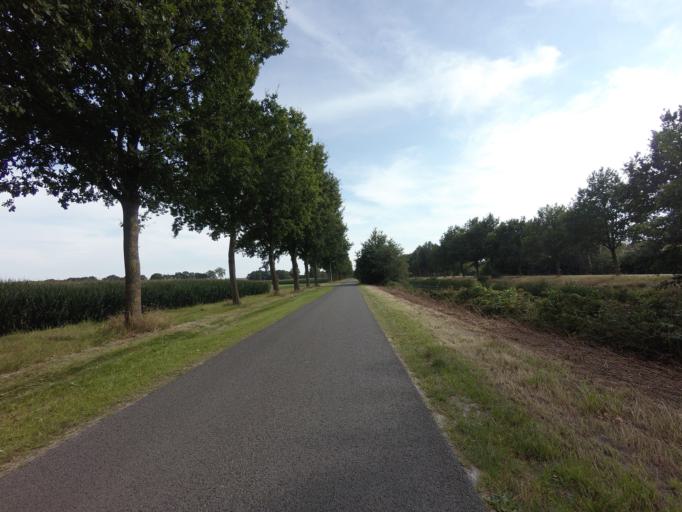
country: NL
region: Drenthe
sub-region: Gemeente Coevorden
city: Coevorden
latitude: 52.6839
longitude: 6.7136
